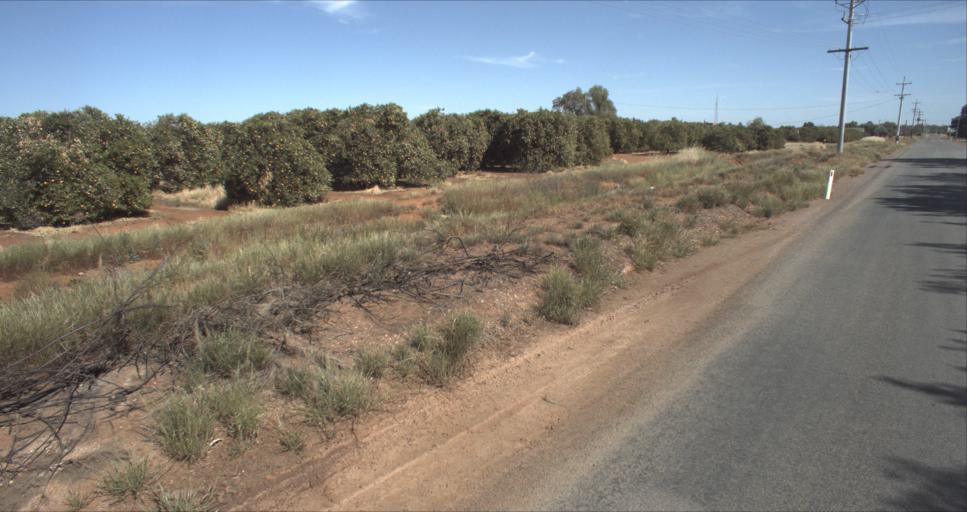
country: AU
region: New South Wales
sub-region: Leeton
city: Leeton
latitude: -34.5879
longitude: 146.4731
